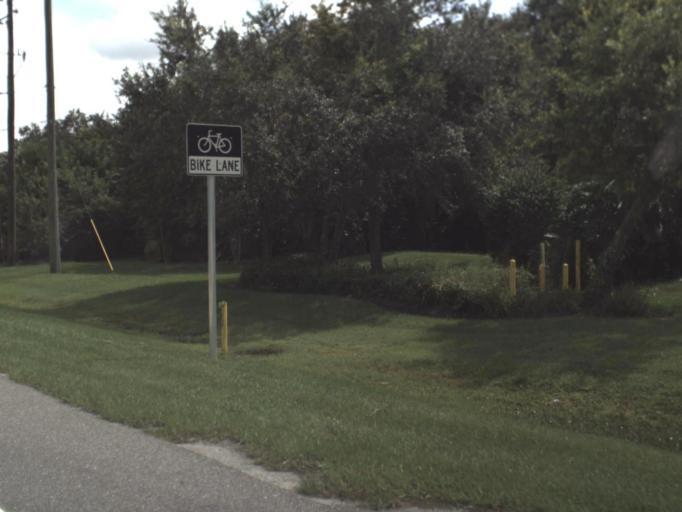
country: US
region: Florida
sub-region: Sarasota County
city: Lake Sarasota
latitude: 27.2674
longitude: -82.4170
